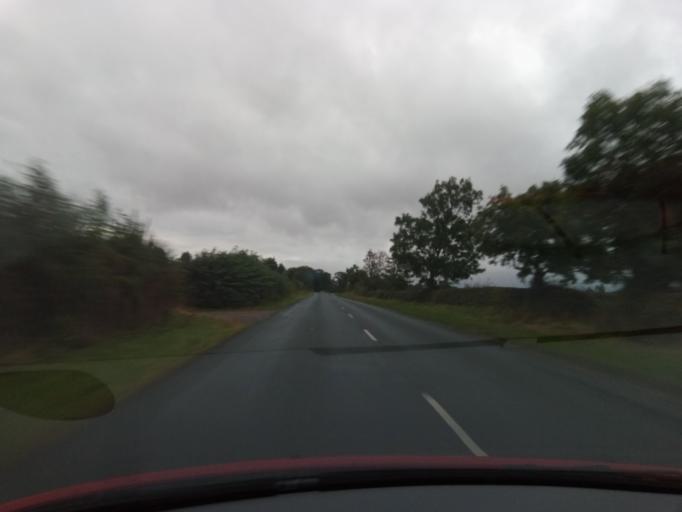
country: GB
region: England
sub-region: Darlington
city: High Coniscliffe
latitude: 54.5130
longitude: -1.6714
